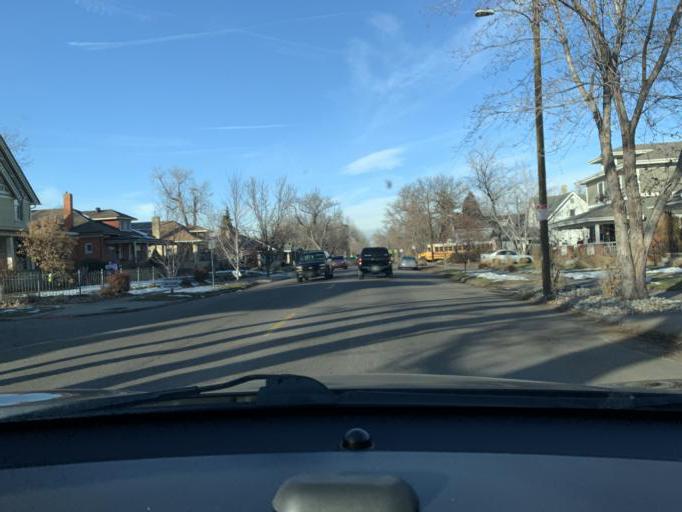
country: US
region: Colorado
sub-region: Adams County
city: Berkley
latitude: 39.7712
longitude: -105.0346
